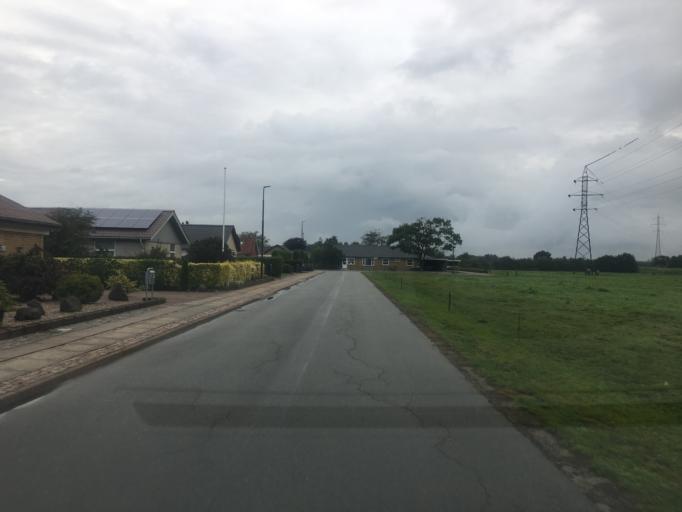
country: DK
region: South Denmark
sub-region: Tonder Kommune
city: Tonder
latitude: 54.9428
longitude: 8.8844
